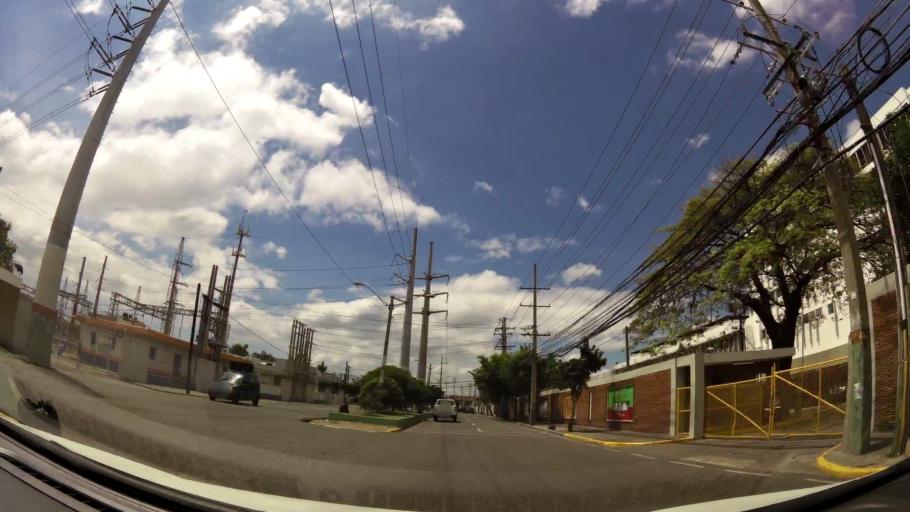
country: DO
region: Nacional
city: Bella Vista
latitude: 18.4416
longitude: -69.9434
